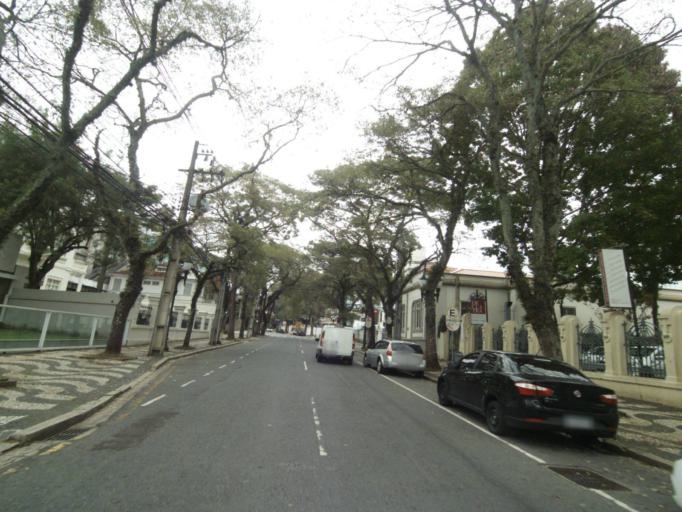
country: BR
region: Parana
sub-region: Curitiba
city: Curitiba
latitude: -25.4380
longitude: -49.2814
